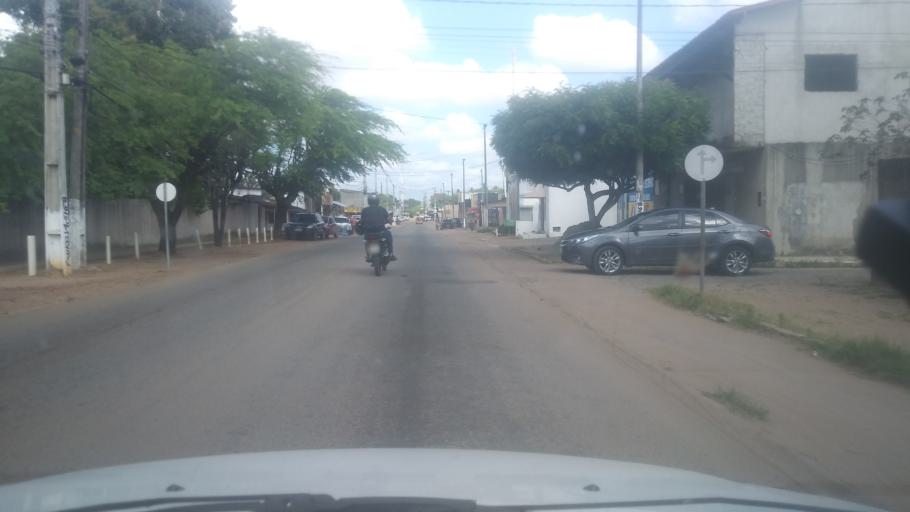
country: BR
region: Rio Grande do Norte
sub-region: Extremoz
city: Extremoz
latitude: -5.7059
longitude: -35.3012
